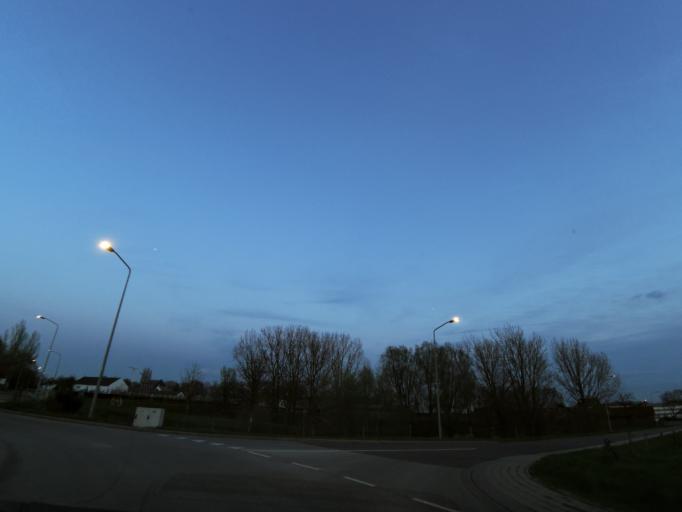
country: NL
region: Limburg
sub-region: Gemeente Simpelveld
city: Simpelveld
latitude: 50.8456
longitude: 5.9990
